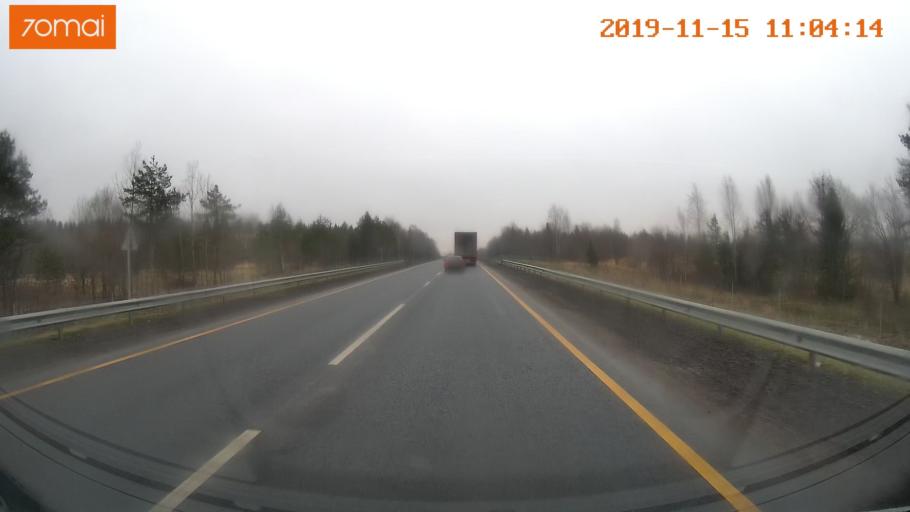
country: RU
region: Vologda
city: Chebsara
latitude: 59.1211
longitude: 38.9792
